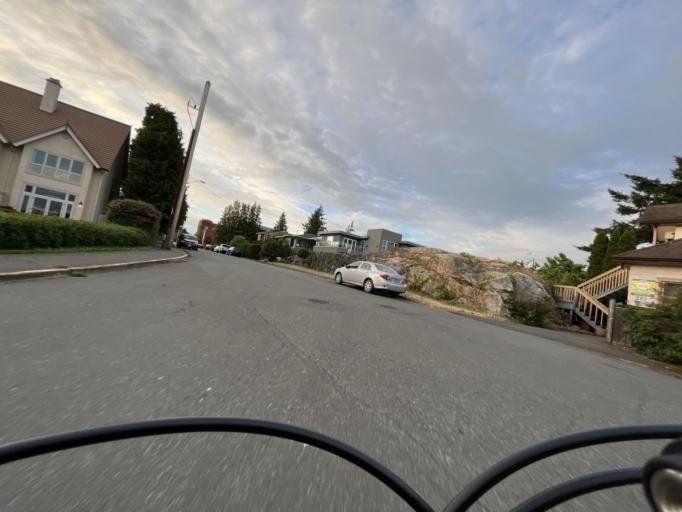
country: CA
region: British Columbia
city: Victoria
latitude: 48.4283
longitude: -123.3872
